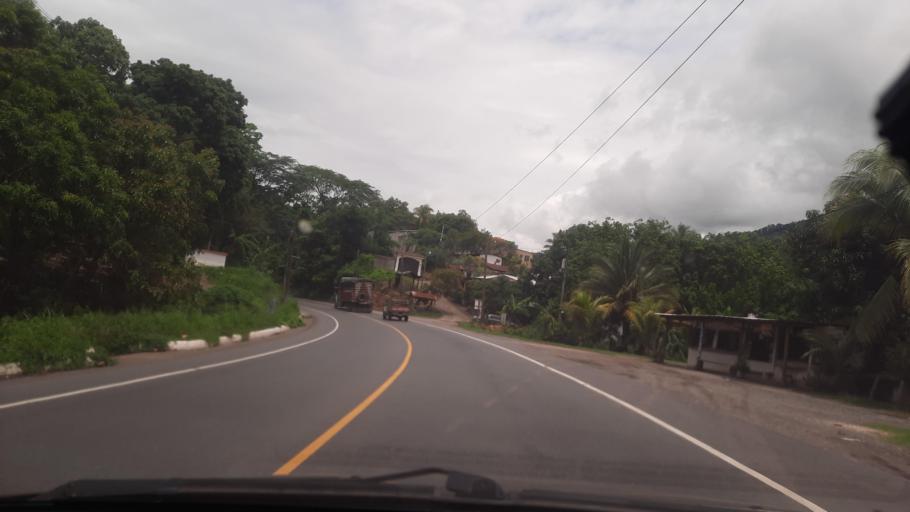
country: GT
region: Zacapa
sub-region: Municipio de Zacapa
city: Gualan
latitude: 15.1977
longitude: -89.2741
